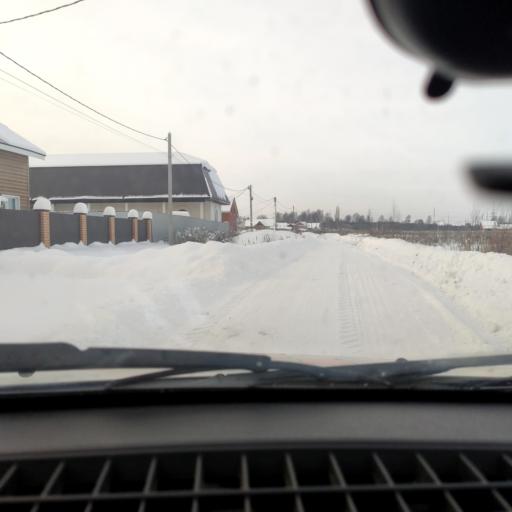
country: RU
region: Bashkortostan
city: Mikhaylovka
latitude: 54.7849
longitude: 55.8183
